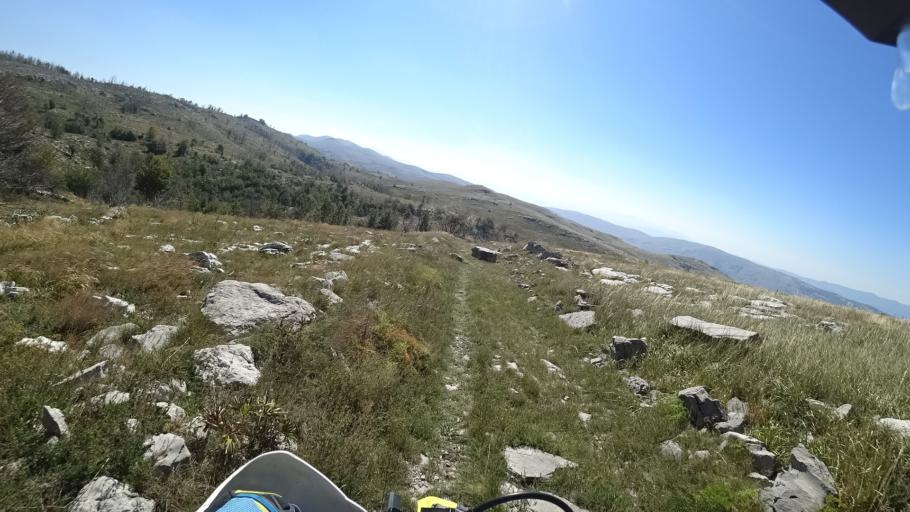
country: HR
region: Splitsko-Dalmatinska
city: Hrvace
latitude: 43.9127
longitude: 16.6101
